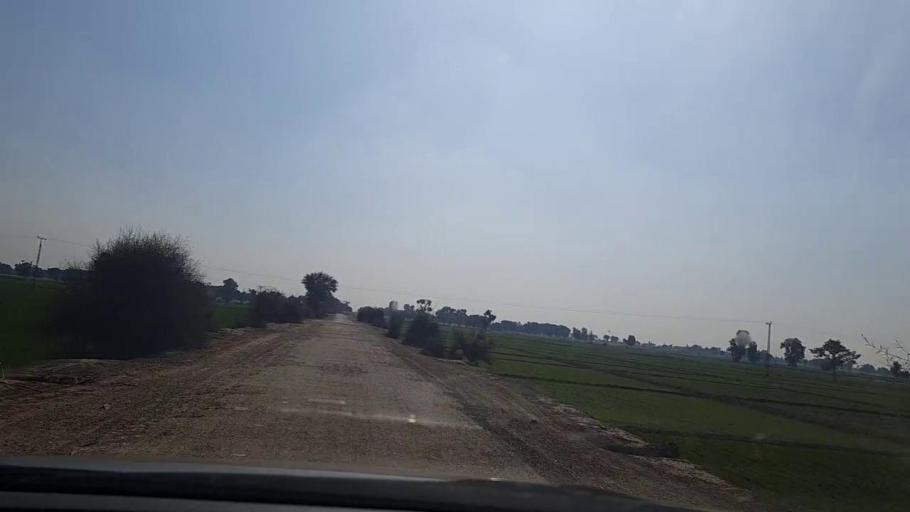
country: PK
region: Sindh
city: Daulatpur
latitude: 26.2887
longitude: 68.0678
